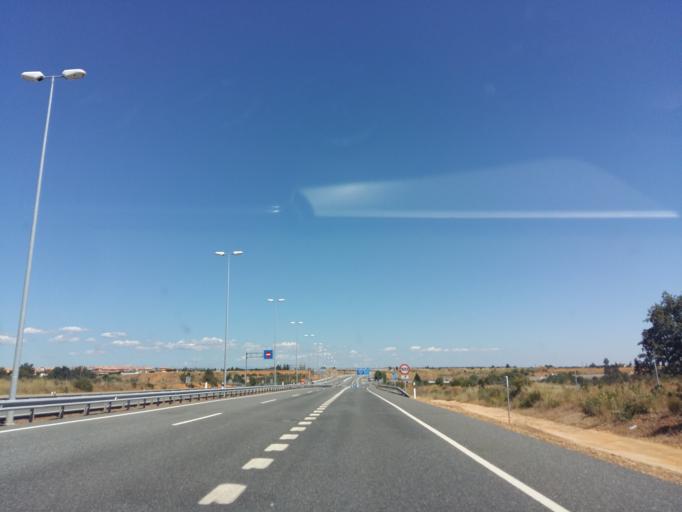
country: ES
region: Castille and Leon
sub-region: Provincia de Leon
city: Valverde de la Virgen
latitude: 42.5660
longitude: -5.6609
